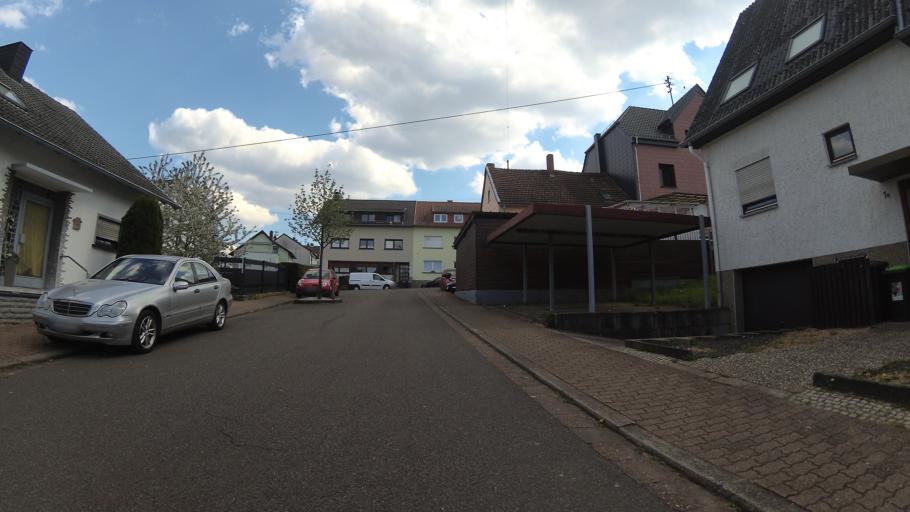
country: DE
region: Saarland
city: Riegelsberg
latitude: 49.3019
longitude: 6.9356
